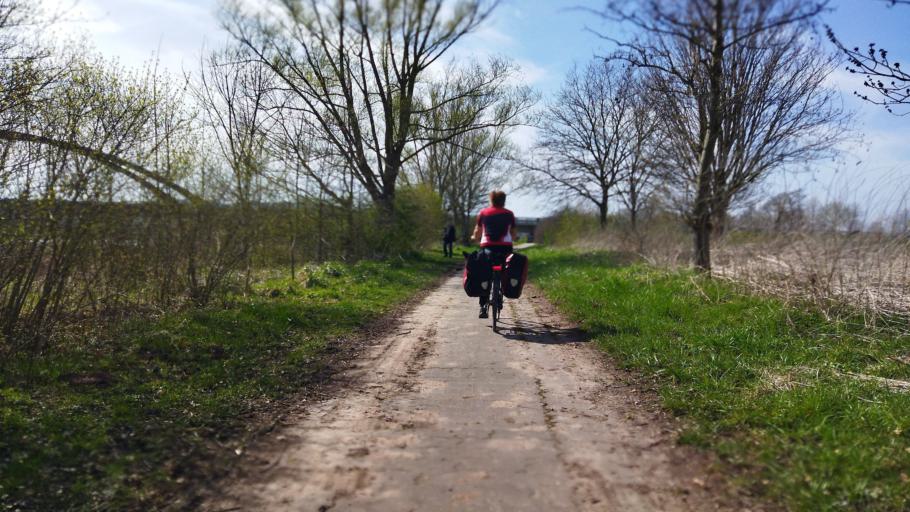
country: DE
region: Lower Saxony
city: Hessisch Oldendorf
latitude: 52.1590
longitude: 9.2518
